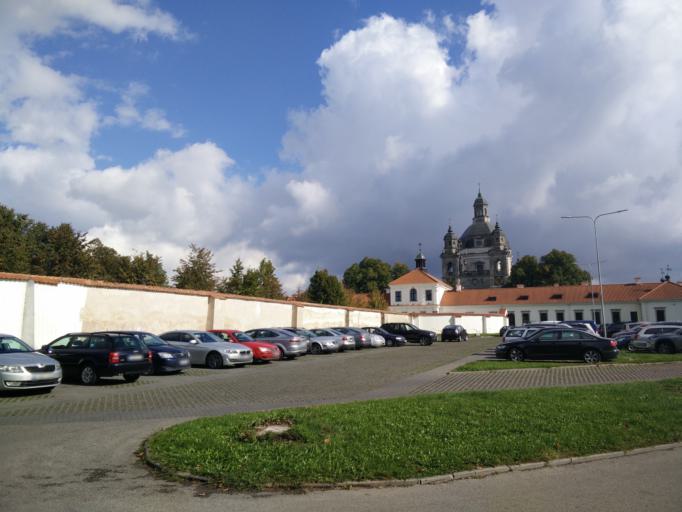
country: LT
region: Kauno apskritis
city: Dainava (Kaunas)
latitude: 54.8760
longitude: 24.0192
